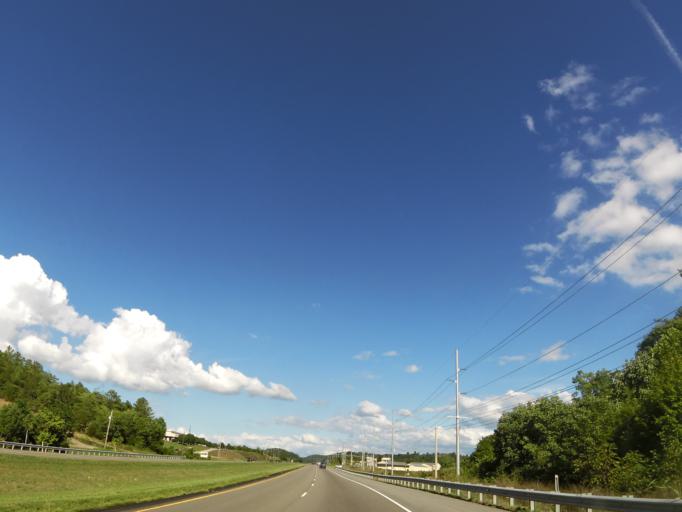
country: US
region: Tennessee
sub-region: Greene County
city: Mosheim
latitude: 36.1730
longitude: -82.9126
